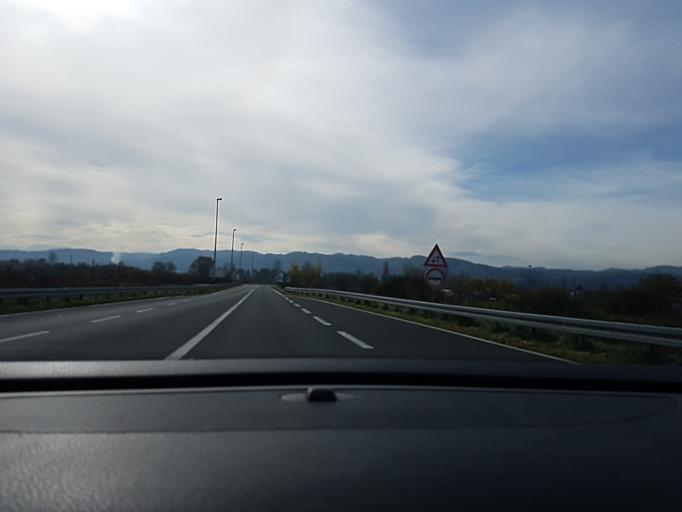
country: HR
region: Zagrebacka
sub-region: Grad Samobor
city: Samobor
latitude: 45.8307
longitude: 15.7201
